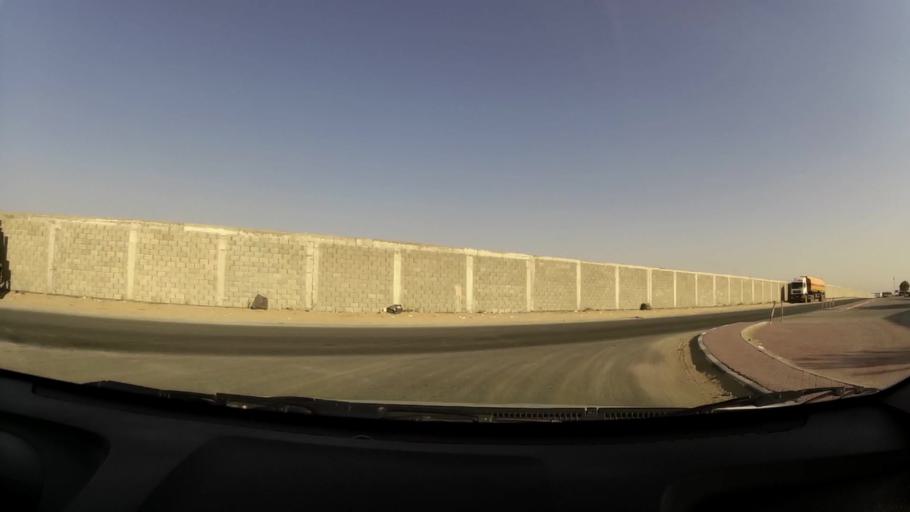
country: AE
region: Umm al Qaywayn
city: Umm al Qaywayn
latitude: 25.4312
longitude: 55.5691
